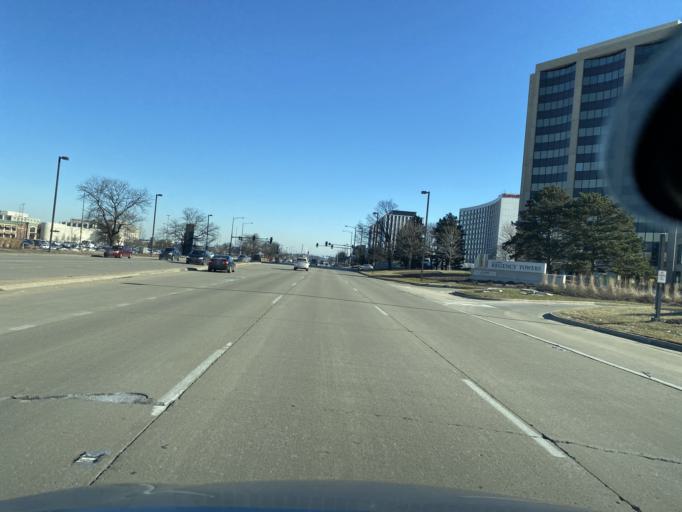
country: US
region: Illinois
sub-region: DuPage County
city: Oakbrook Terrace
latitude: 41.8466
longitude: -87.9559
